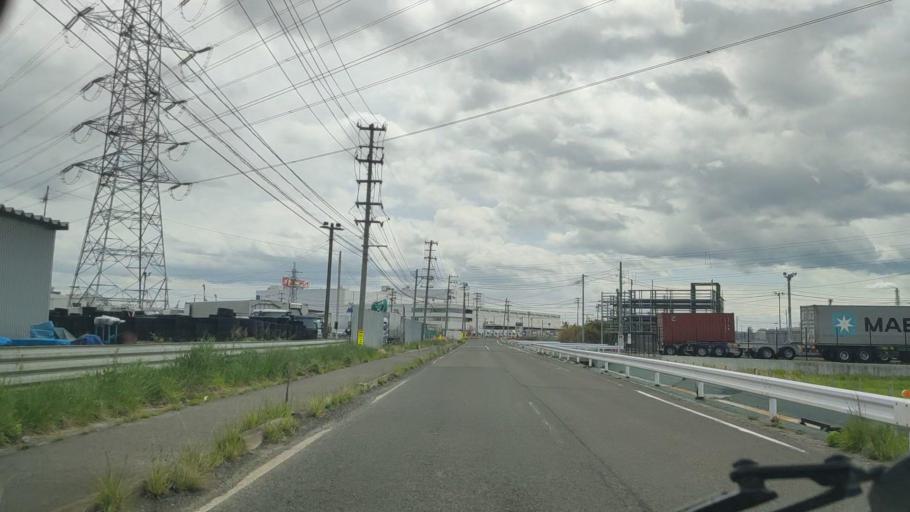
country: JP
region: Miyagi
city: Shiogama
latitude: 38.2785
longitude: 141.0094
